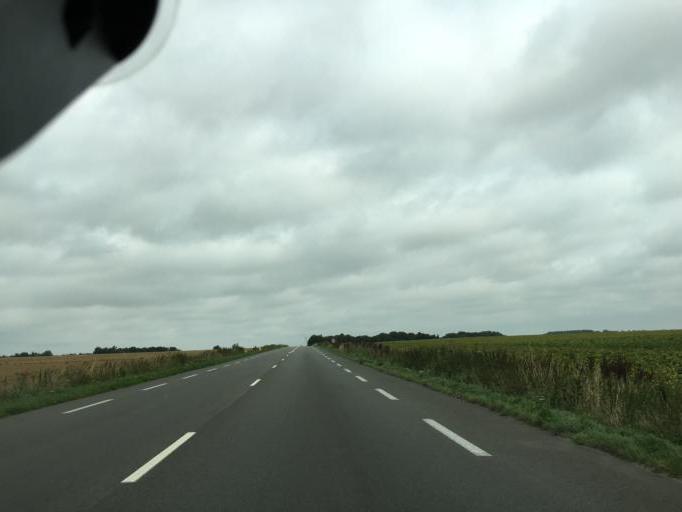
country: FR
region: Nord-Pas-de-Calais
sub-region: Departement du Pas-de-Calais
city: Saint-Pol-sur-Ternoise
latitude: 50.3954
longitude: 2.3562
